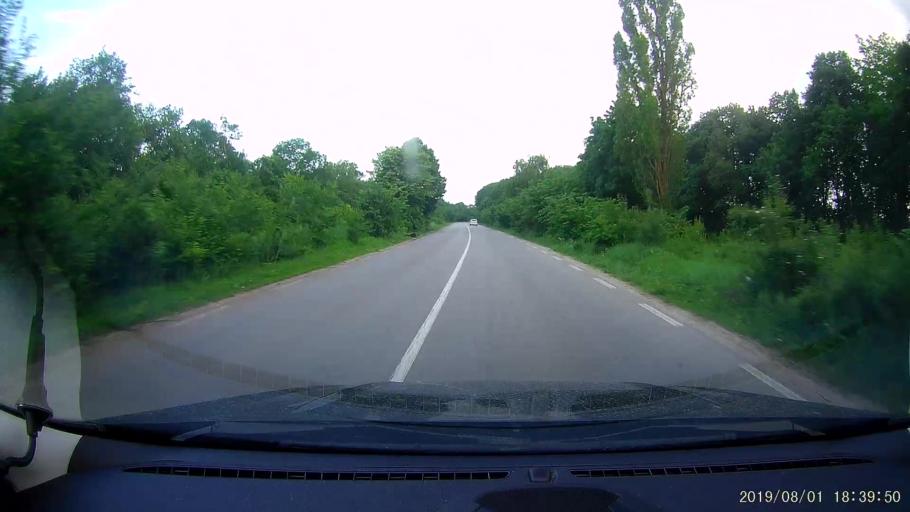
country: BG
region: Shumen
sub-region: Obshtina Khitrino
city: Gara Khitrino
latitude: 43.3776
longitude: 26.9186
